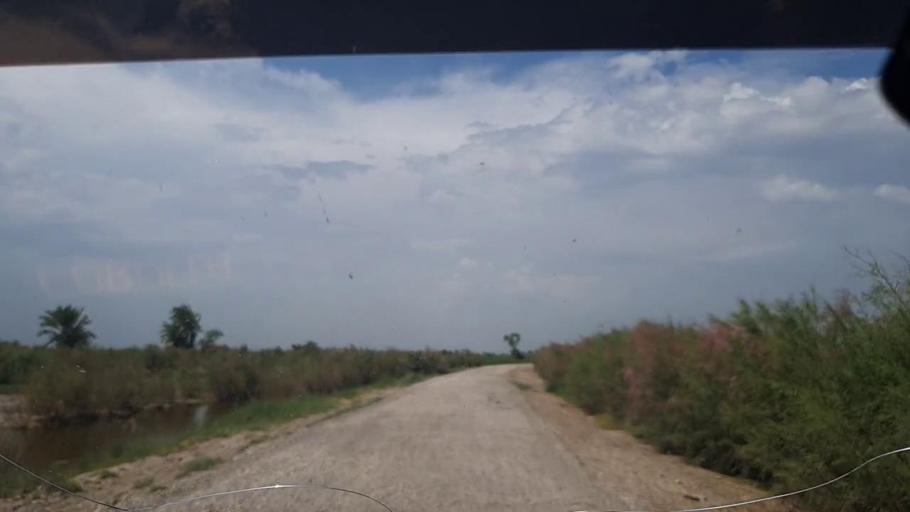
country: PK
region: Sindh
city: Ghauspur
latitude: 28.1473
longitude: 68.9809
